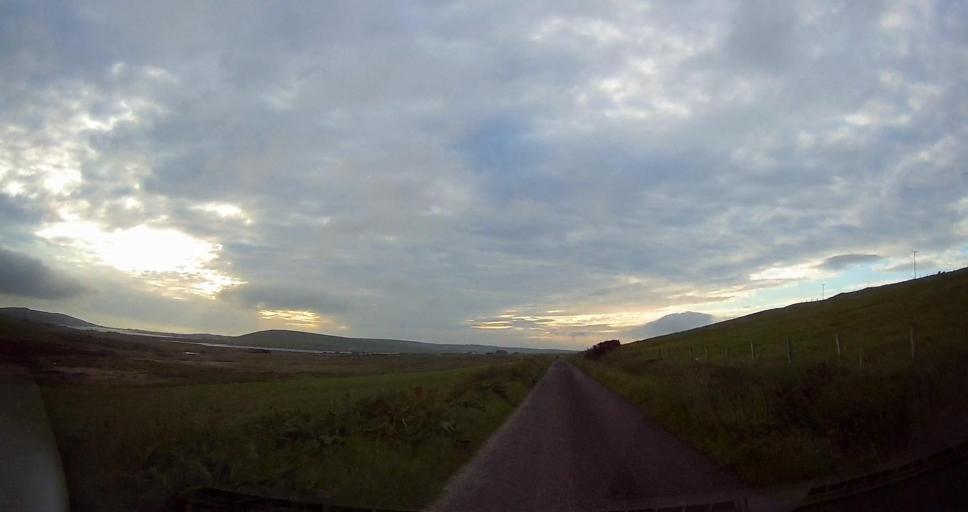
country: GB
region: Scotland
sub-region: Orkney Islands
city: Stromness
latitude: 59.1026
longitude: -3.2110
